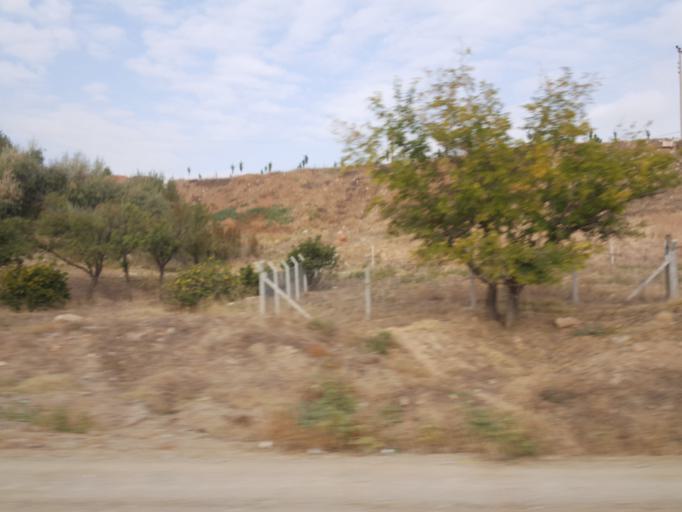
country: TR
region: Kirikkale
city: Bahsili
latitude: 39.8053
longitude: 33.4668
